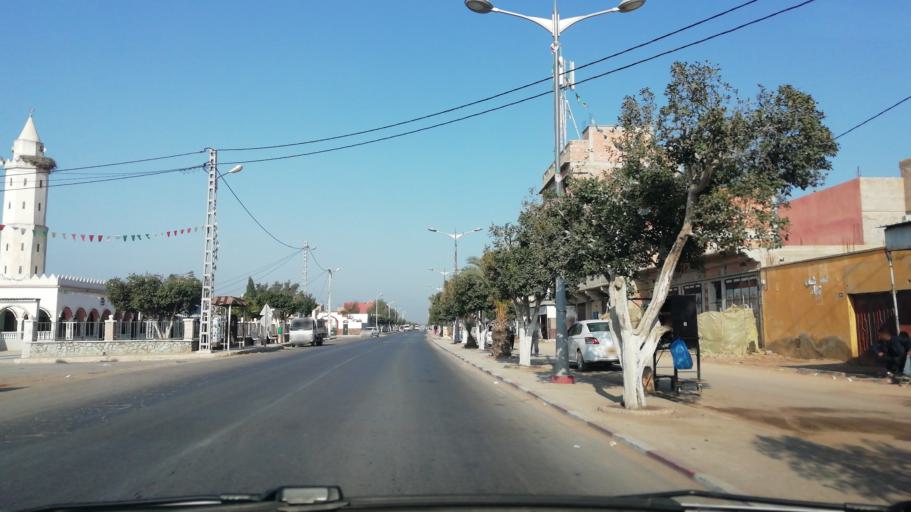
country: DZ
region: Mostaganem
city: Mostaganem
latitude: 35.7523
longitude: 0.1204
